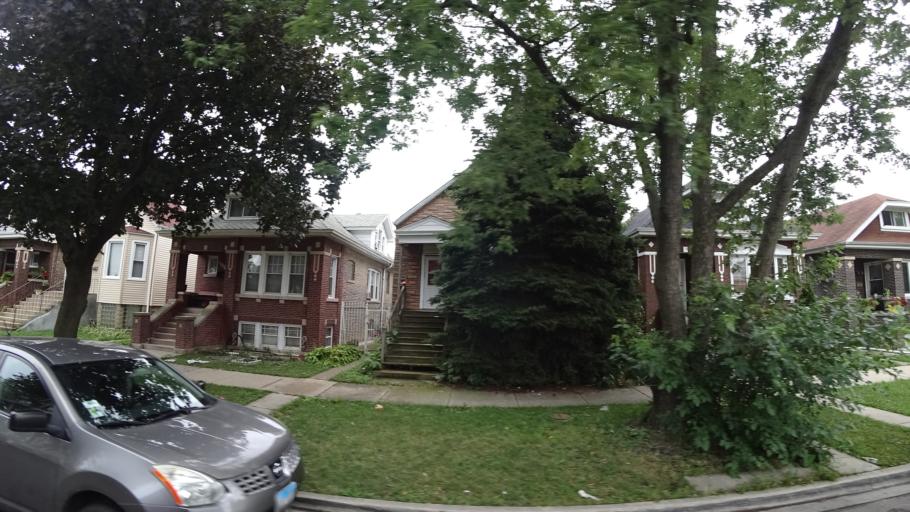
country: US
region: Illinois
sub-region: Cook County
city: Cicero
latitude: 41.8560
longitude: -87.7665
